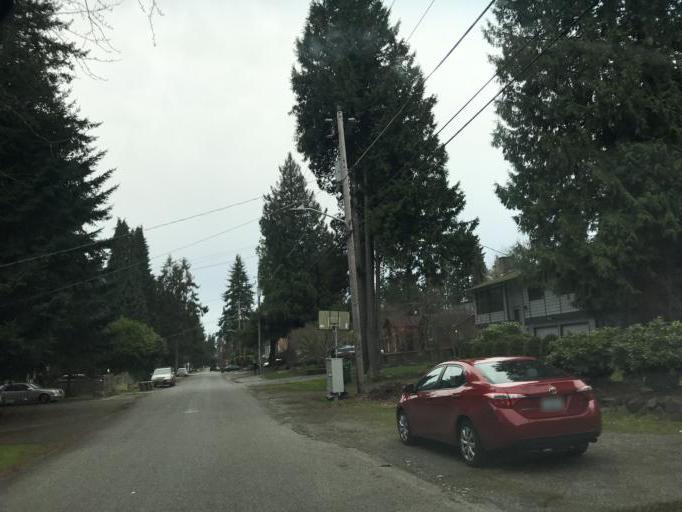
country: US
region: Washington
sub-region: King County
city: Lake Forest Park
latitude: 47.7098
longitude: -122.3062
